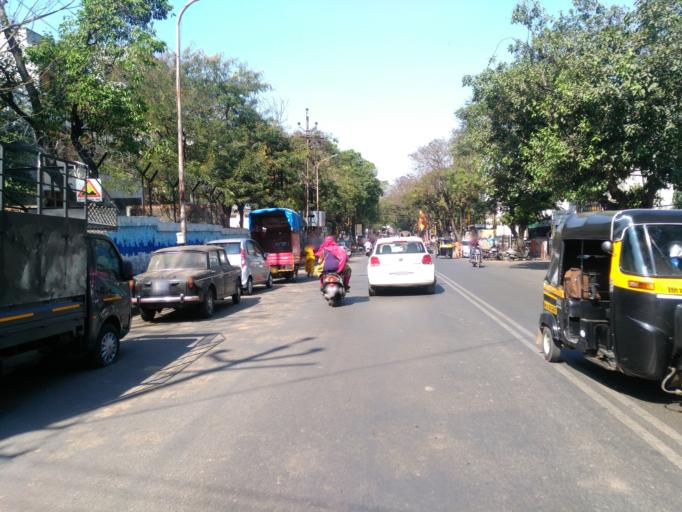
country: IN
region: Maharashtra
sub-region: Pune Division
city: Pune
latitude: 18.4864
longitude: 73.8500
